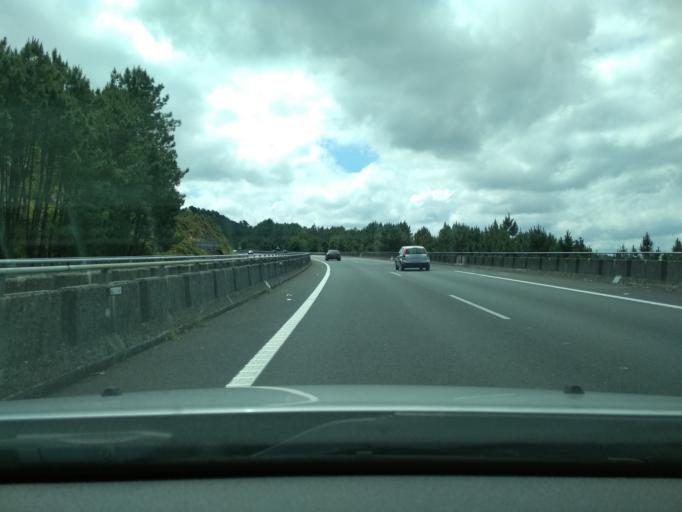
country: ES
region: Galicia
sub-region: Provincia de Pontevedra
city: Portas
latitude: 42.5855
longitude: -8.6759
